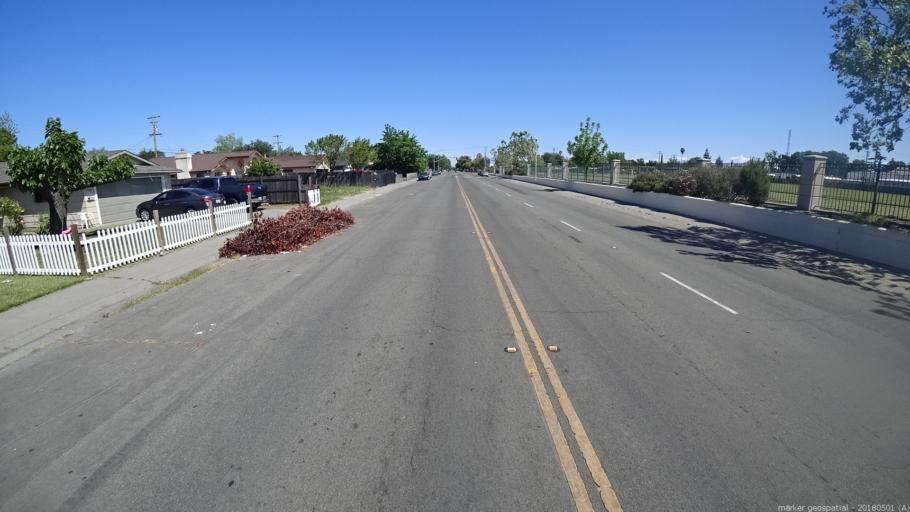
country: US
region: California
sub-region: Sacramento County
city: Rio Linda
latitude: 38.6350
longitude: -121.4385
